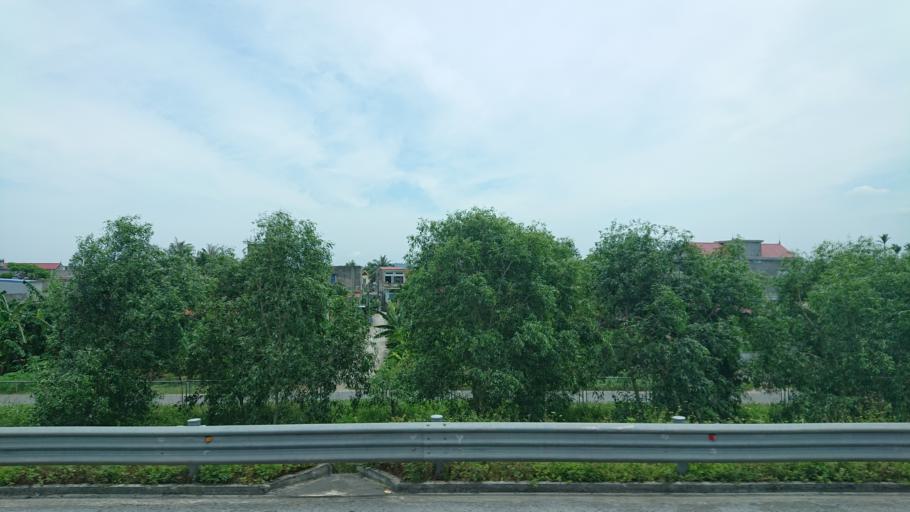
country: VN
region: Hai Phong
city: Nui Doi
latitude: 20.7682
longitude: 106.6347
